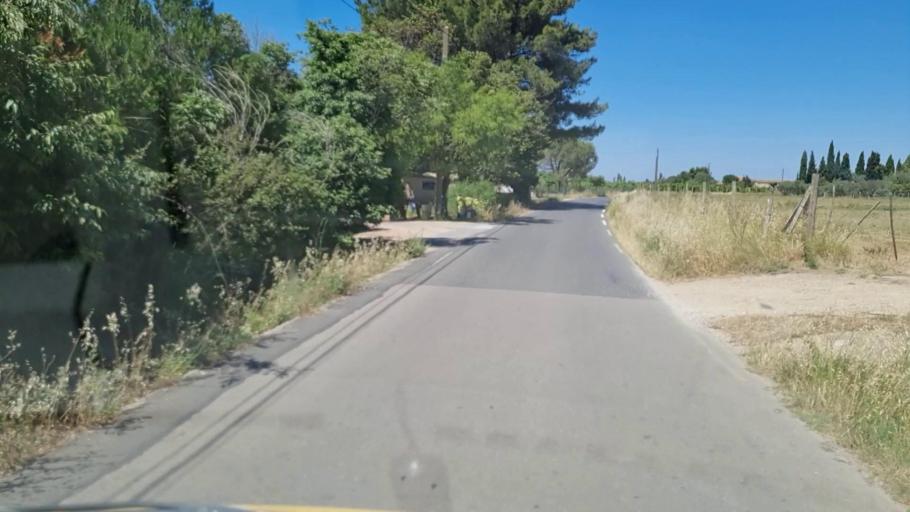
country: FR
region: Languedoc-Roussillon
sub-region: Departement du Gard
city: Le Cailar
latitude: 43.6636
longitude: 4.2576
